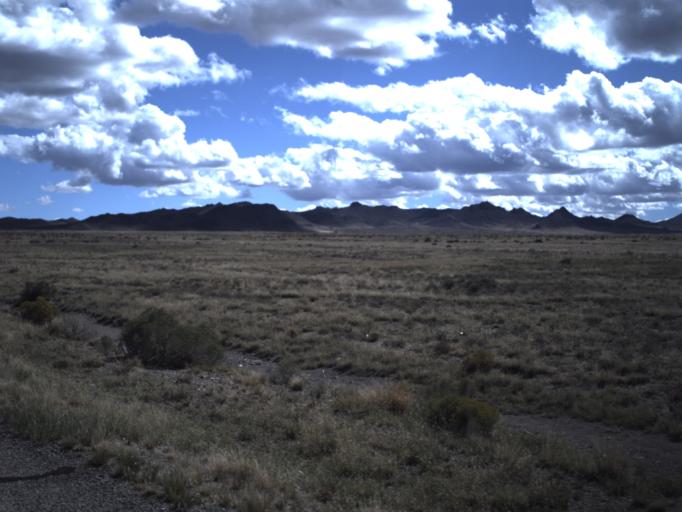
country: US
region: Utah
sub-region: Beaver County
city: Milford
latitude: 38.4516
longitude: -113.3491
